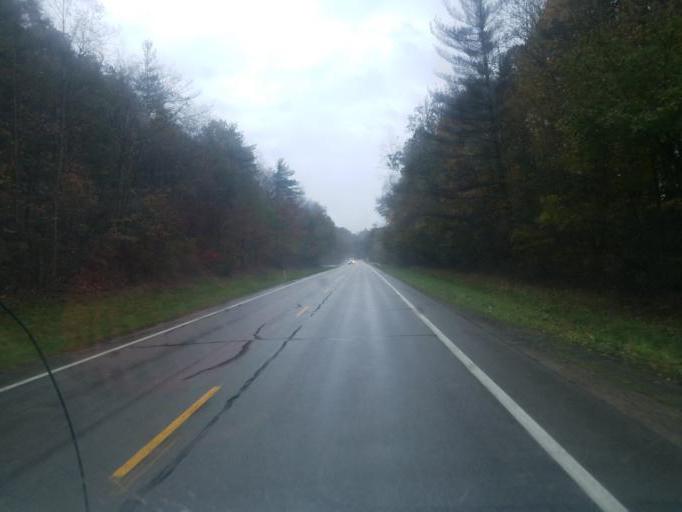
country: US
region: Ohio
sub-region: Muskingum County
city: North Zanesville
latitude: 40.0187
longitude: -82.0900
